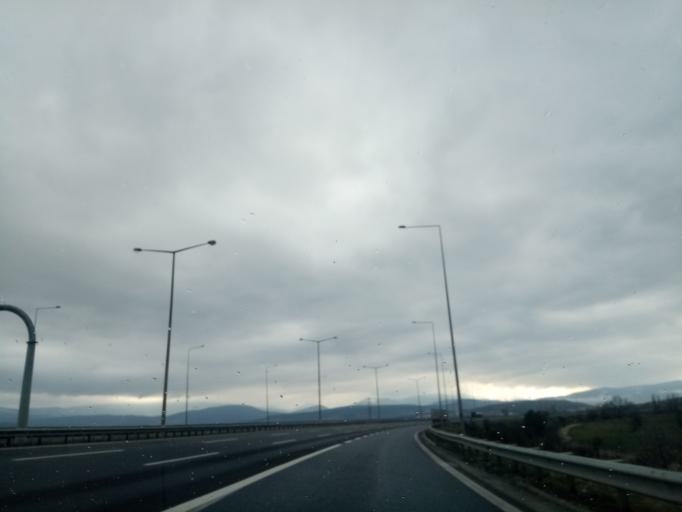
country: TR
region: Bolu
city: Bolu
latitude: 40.7173
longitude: 31.5210
